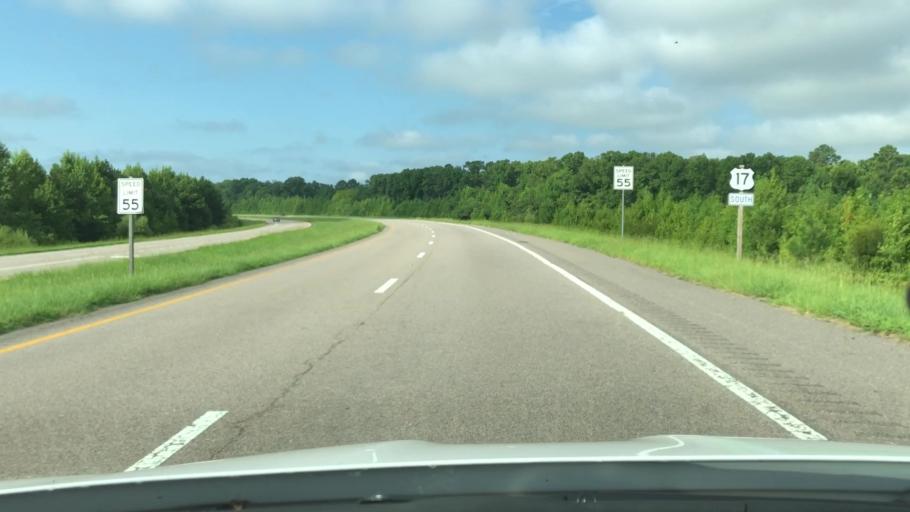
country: US
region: Virginia
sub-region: City of Portsmouth
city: Portsmouth Heights
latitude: 36.6137
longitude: -76.3762
